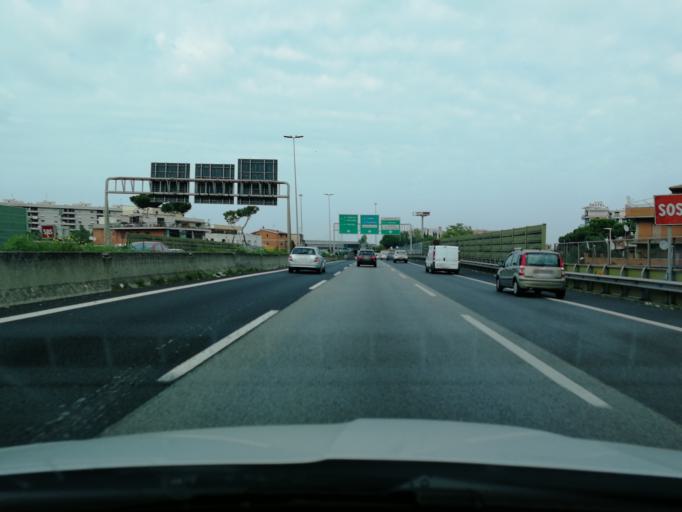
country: IT
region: Latium
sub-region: Citta metropolitana di Roma Capitale
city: Ciampino
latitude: 41.8452
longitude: 12.5945
